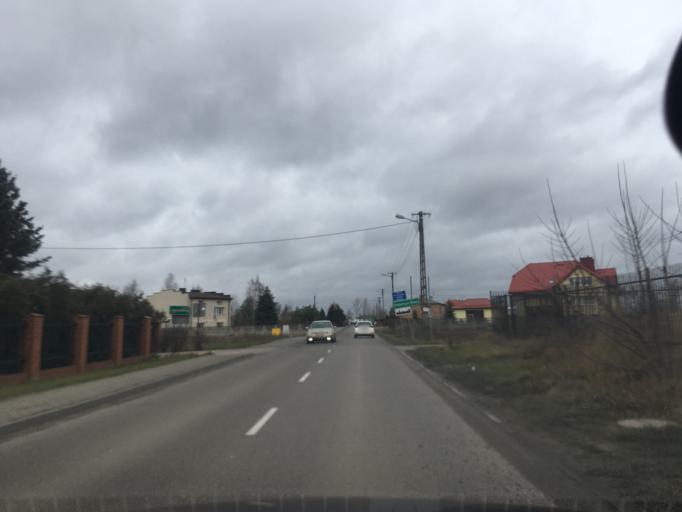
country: PL
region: Masovian Voivodeship
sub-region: Powiat piaseczynski
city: Lesznowola
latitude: 52.1192
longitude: 20.9303
